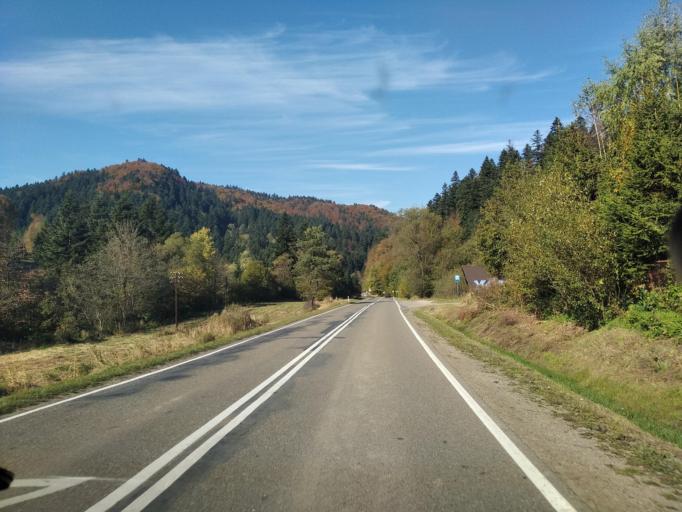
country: PL
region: Subcarpathian Voivodeship
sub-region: Powiat leski
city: Baligrod
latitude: 49.3140
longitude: 22.2755
